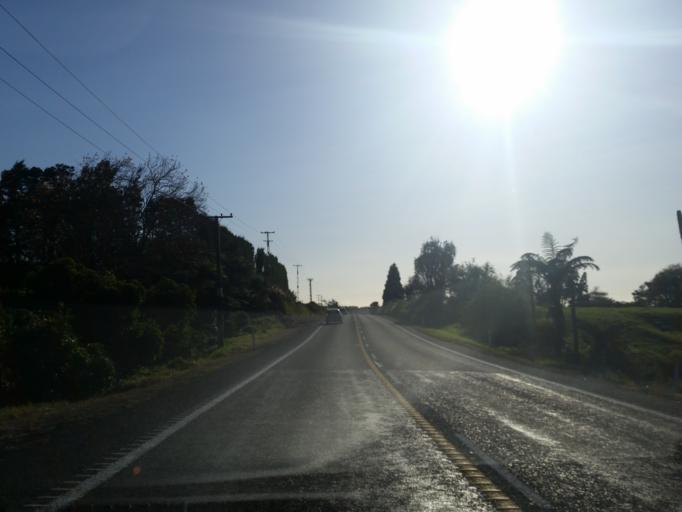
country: NZ
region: Bay of Plenty
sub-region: Western Bay of Plenty District
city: Katikati
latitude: -37.4794
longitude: 175.9309
